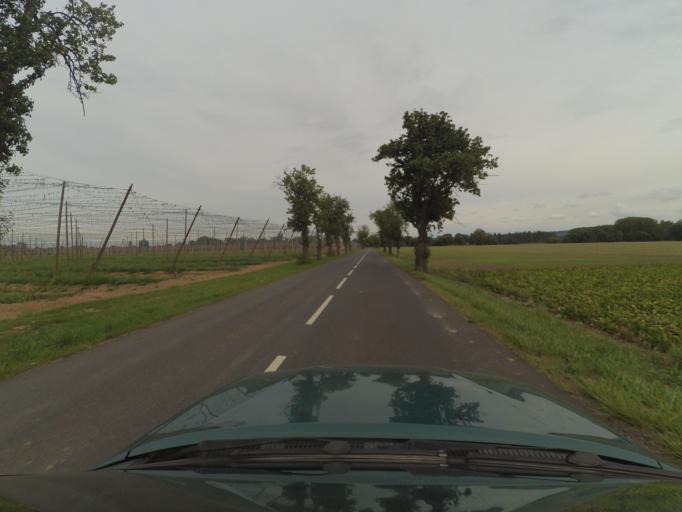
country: CZ
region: Ustecky
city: Cerncice
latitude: 50.3730
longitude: 13.8730
